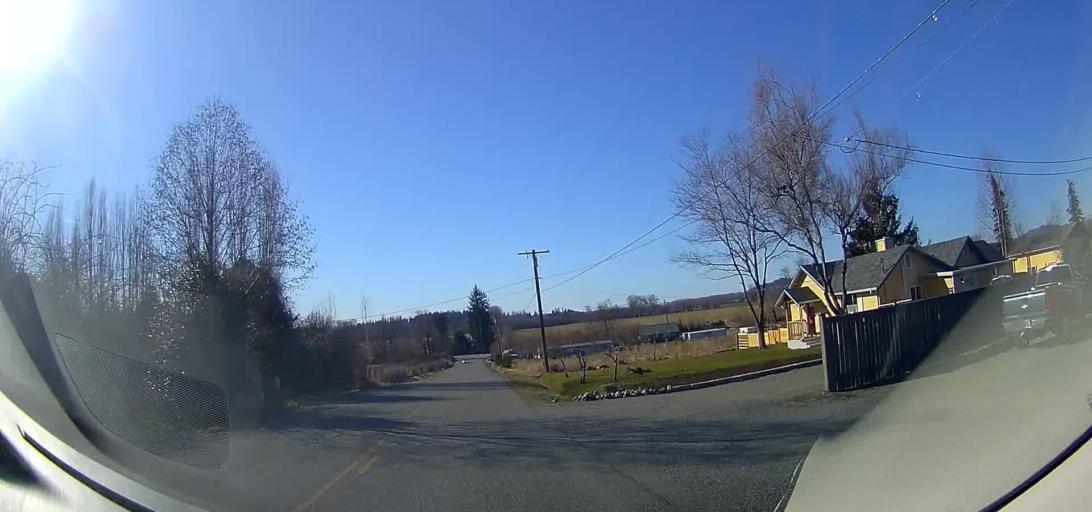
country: US
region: Washington
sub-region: Skagit County
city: Clear Lake
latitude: 48.4570
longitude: -122.2565
